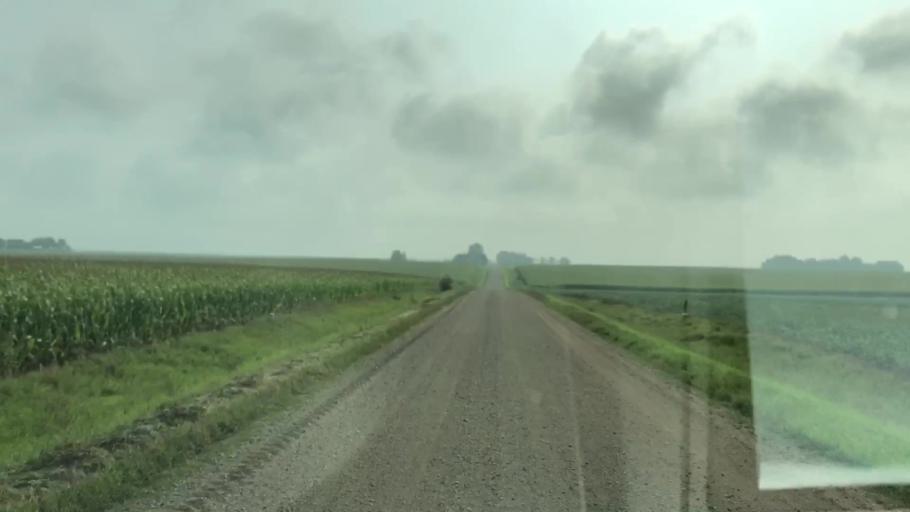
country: US
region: Iowa
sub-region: Sioux County
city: Hull
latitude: 43.2298
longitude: -96.0762
